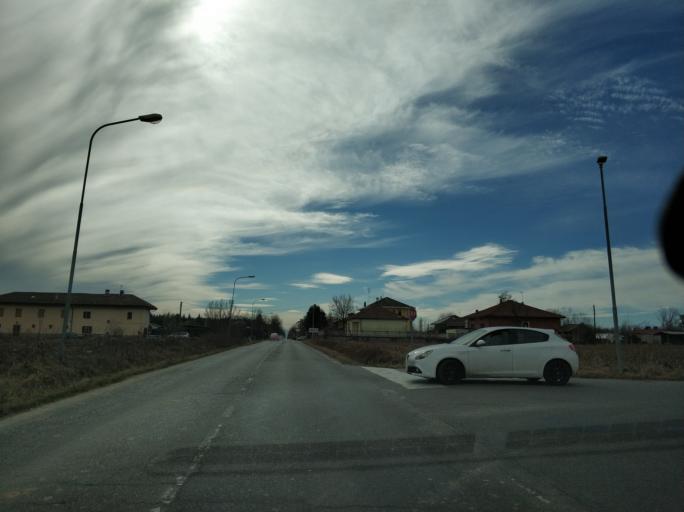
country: IT
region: Piedmont
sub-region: Provincia di Torino
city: Lombardore
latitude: 45.2276
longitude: 7.7318
